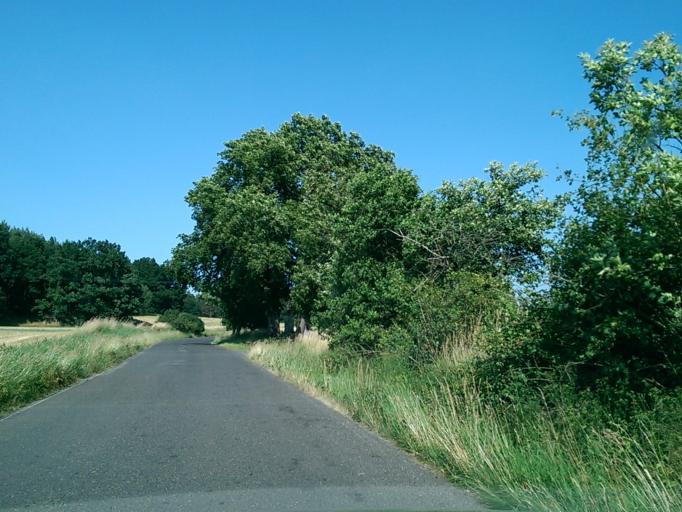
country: CZ
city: Duba
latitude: 50.5423
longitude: 14.4800
